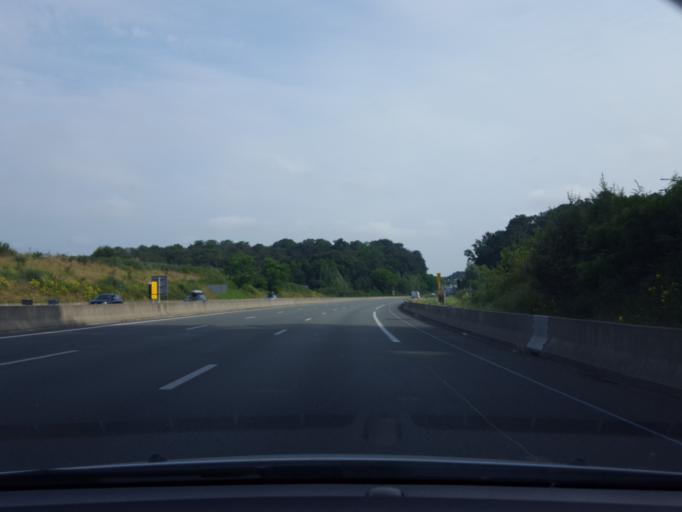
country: FR
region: Aquitaine
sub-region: Departement des Pyrenees-Atlantiques
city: Boucau
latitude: 43.5121
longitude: -1.4435
